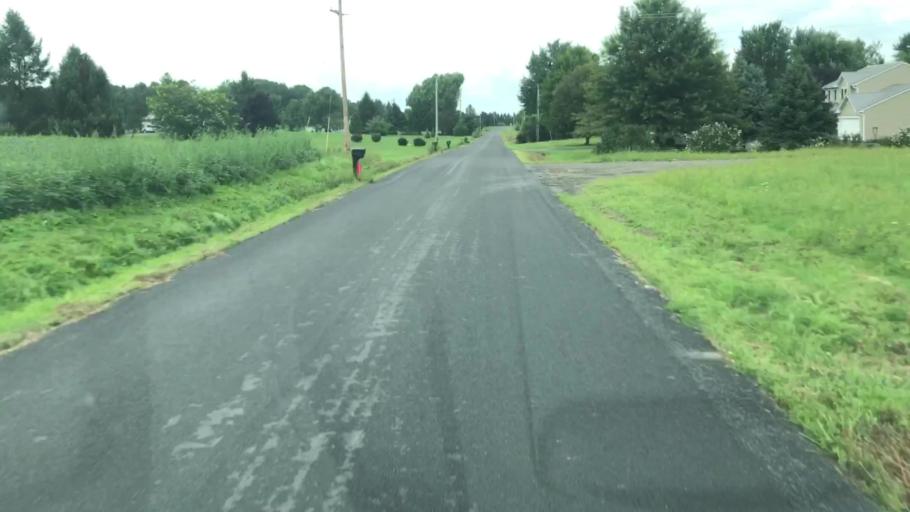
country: US
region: New York
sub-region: Cayuga County
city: Auburn
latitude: 42.9733
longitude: -76.5088
